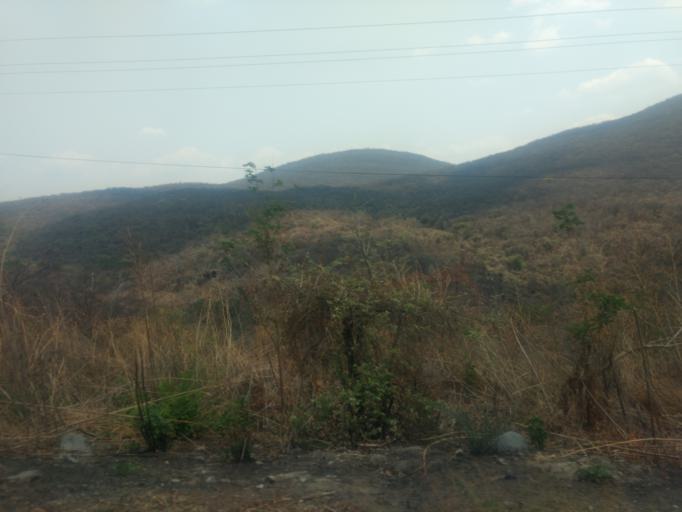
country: MX
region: Morelos
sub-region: Mazatepec
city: Cuauchichinola
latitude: 18.6559
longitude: -99.4102
